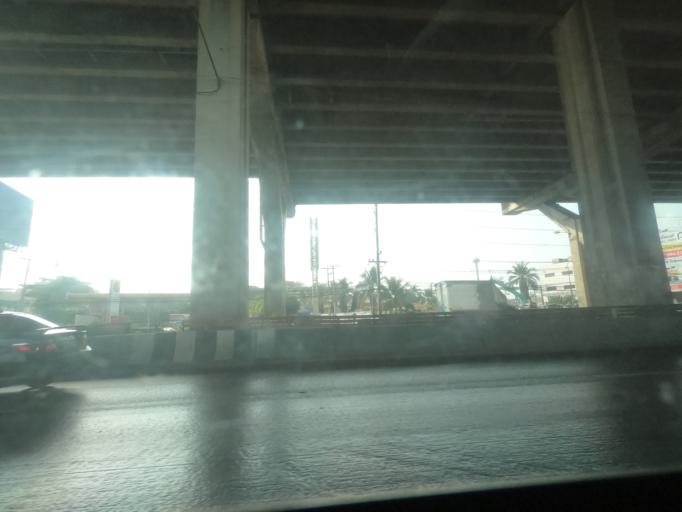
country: TH
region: Bangkok
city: Sai Mai
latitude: 13.9724
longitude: 100.6490
